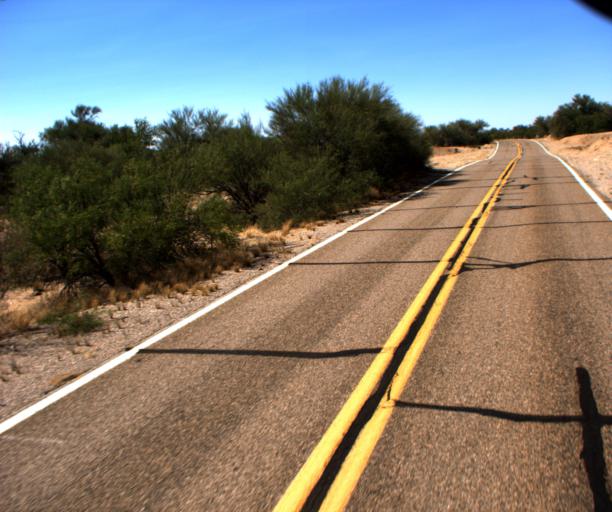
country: US
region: Arizona
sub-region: Pima County
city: Three Points
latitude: 31.9189
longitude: -111.3907
